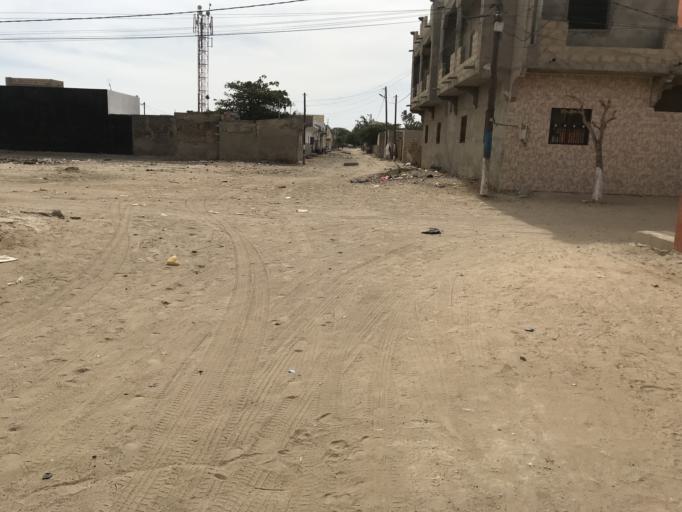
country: SN
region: Saint-Louis
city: Saint-Louis
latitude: 16.0249
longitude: -16.4835
